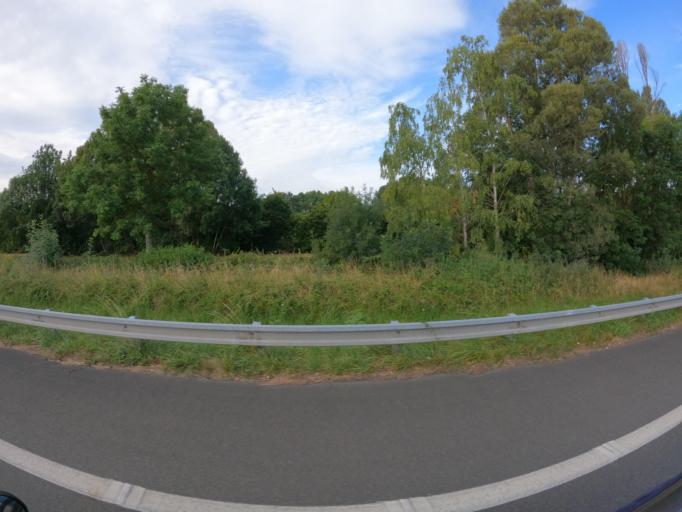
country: FR
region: Centre
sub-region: Departement d'Indre-et-Loire
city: Saint-Nicolas-de-Bourgueil
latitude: 47.2663
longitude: 0.1204
